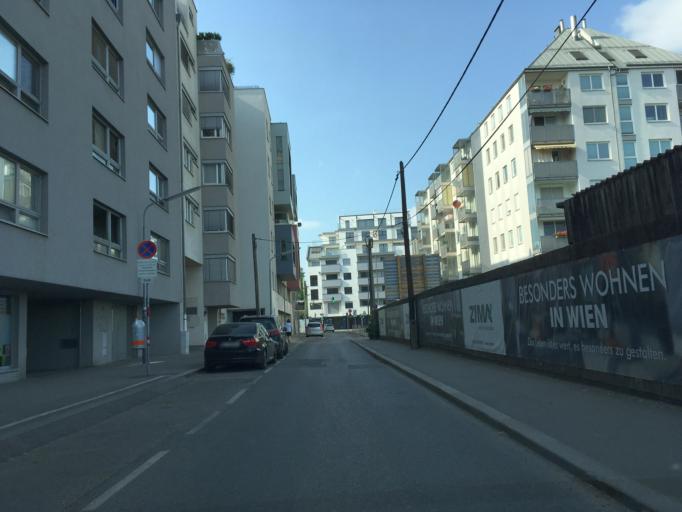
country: AT
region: Lower Austria
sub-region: Politischer Bezirk Wien-Umgebung
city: Gerasdorf bei Wien
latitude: 48.2498
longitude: 16.4344
